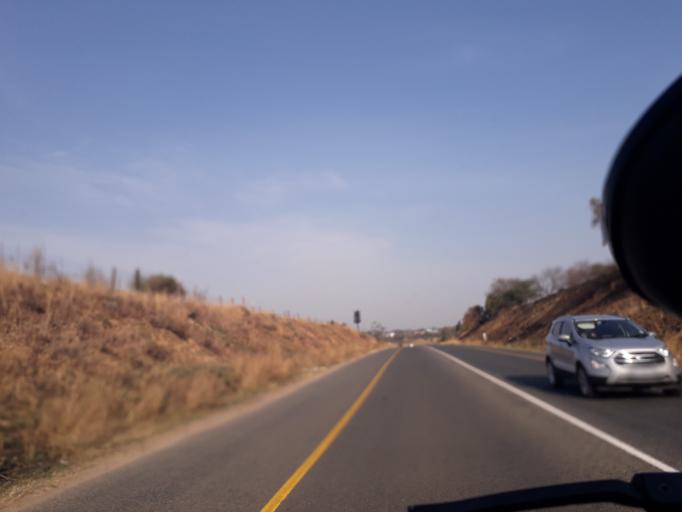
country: ZA
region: Gauteng
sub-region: West Rand District Municipality
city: Muldersdriseloop
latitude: -25.9649
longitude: 27.8995
